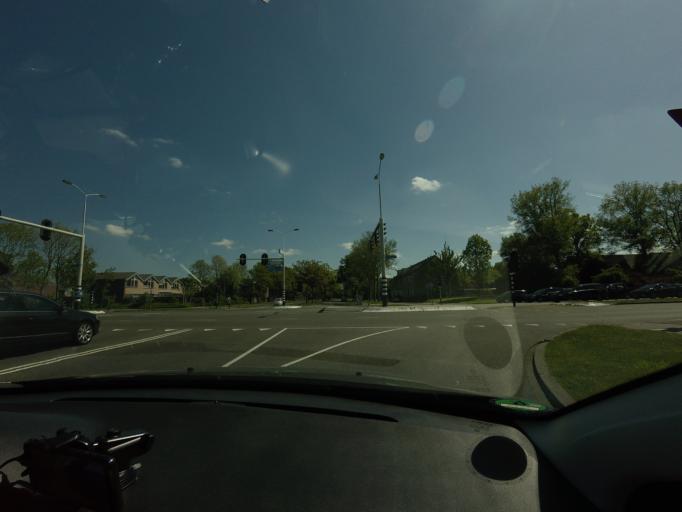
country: NL
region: North Holland
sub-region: Gemeente Langedijk
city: Broek op Langedijk
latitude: 52.6626
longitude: 4.8163
